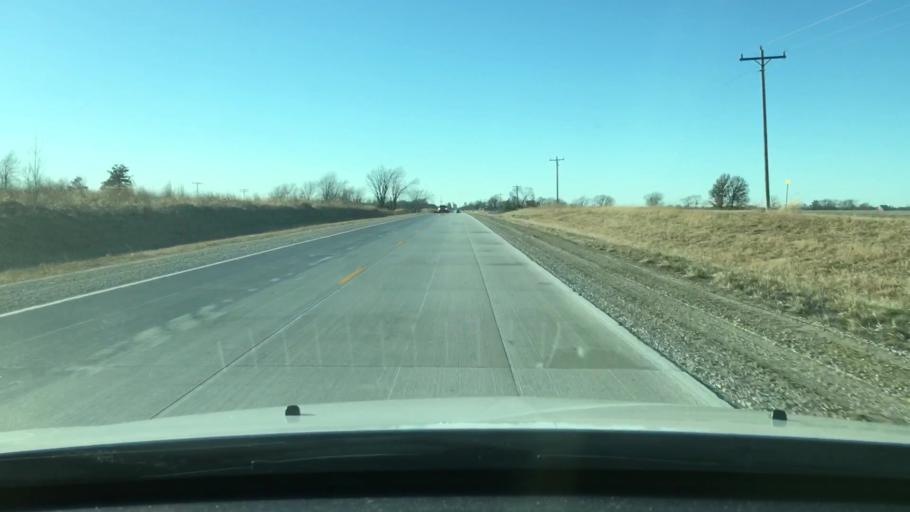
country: US
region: Missouri
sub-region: Boone County
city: Centralia
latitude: 39.2033
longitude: -92.0769
